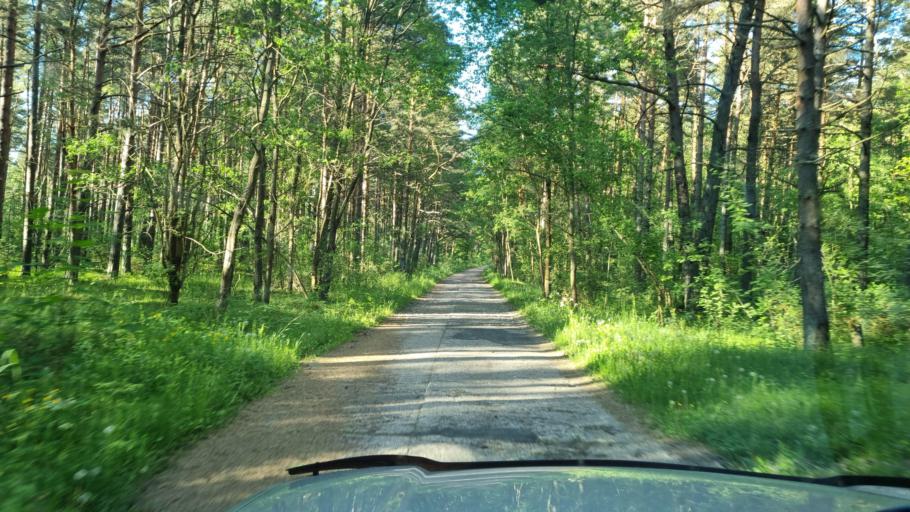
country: LV
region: Ventspils
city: Ventspils
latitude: 57.3739
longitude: 21.5257
